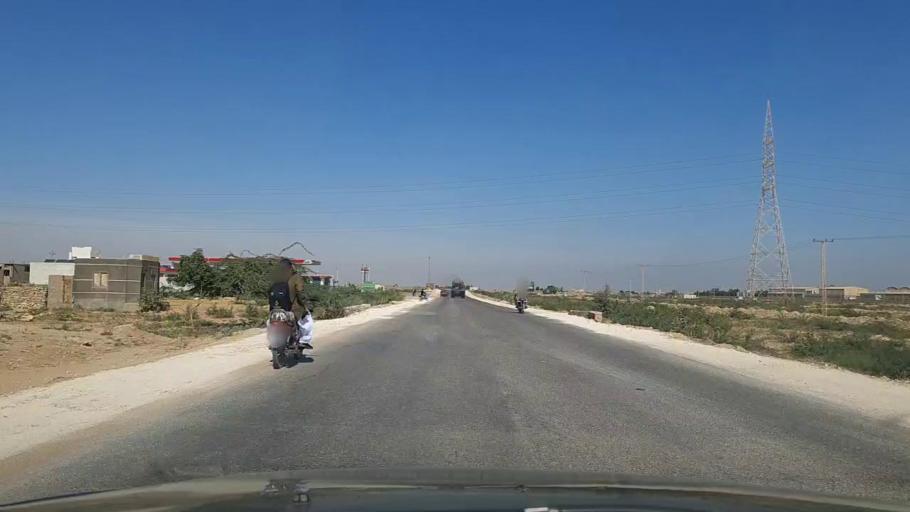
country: PK
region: Sindh
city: Kotri
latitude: 25.3324
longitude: 68.2428
